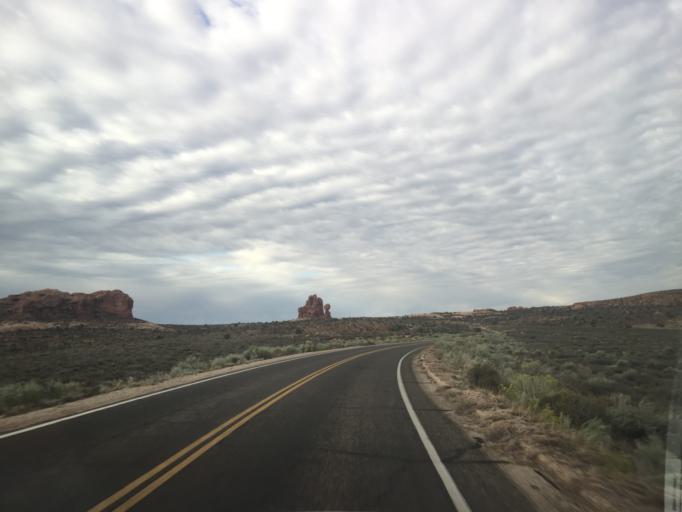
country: US
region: Utah
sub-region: Grand County
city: Moab
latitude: 38.7147
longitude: -109.5567
